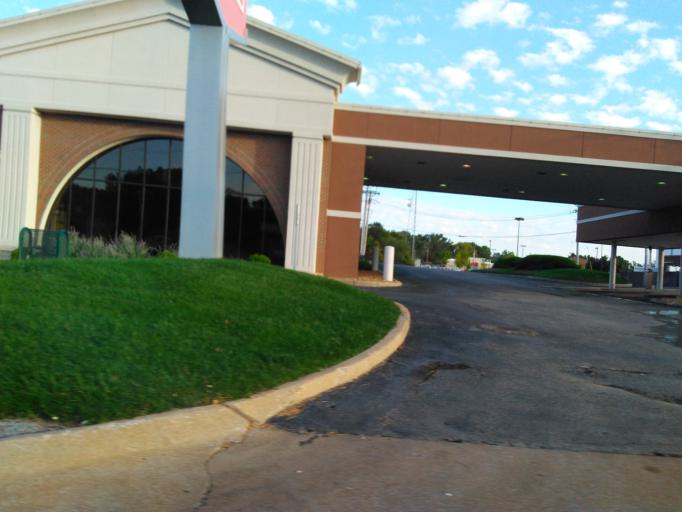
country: US
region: Missouri
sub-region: Saint Louis County
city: Sappington
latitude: 38.5339
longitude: -90.3833
